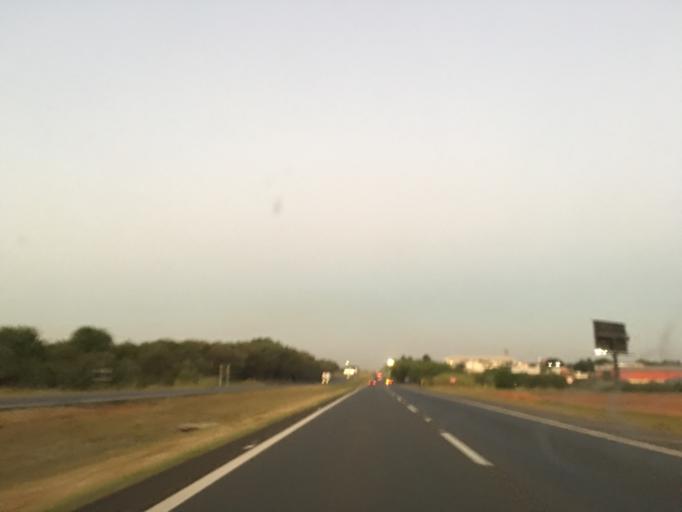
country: BR
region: Sao Paulo
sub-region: Piracicaba
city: Piracicaba
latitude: -22.7218
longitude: -47.6053
